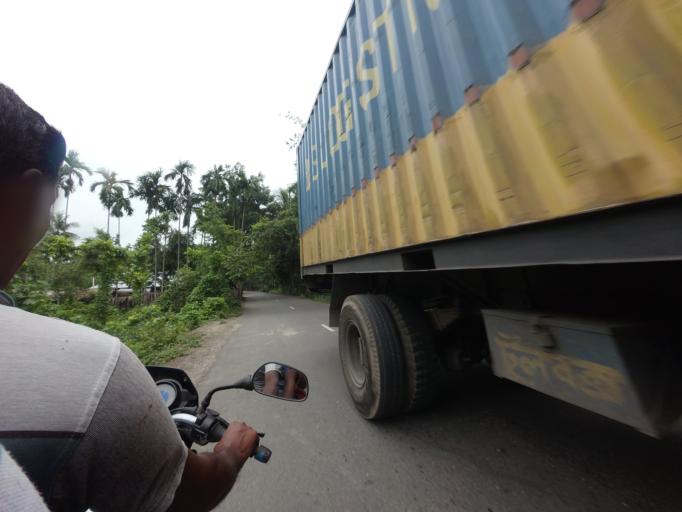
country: BD
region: Khulna
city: Kalia
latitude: 23.1591
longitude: 89.6440
